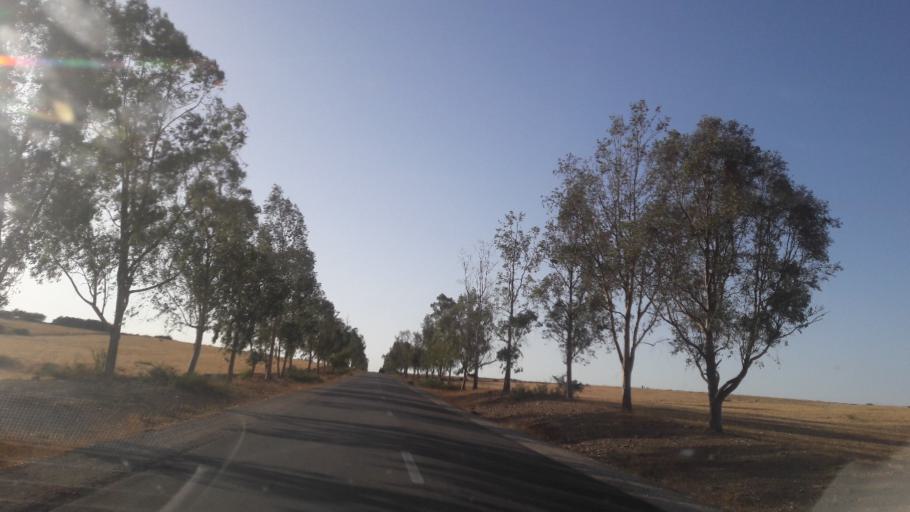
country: MA
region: Chaouia-Ouardigha
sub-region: Khouribga Province
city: Boujniba
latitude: 33.0063
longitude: -6.6871
